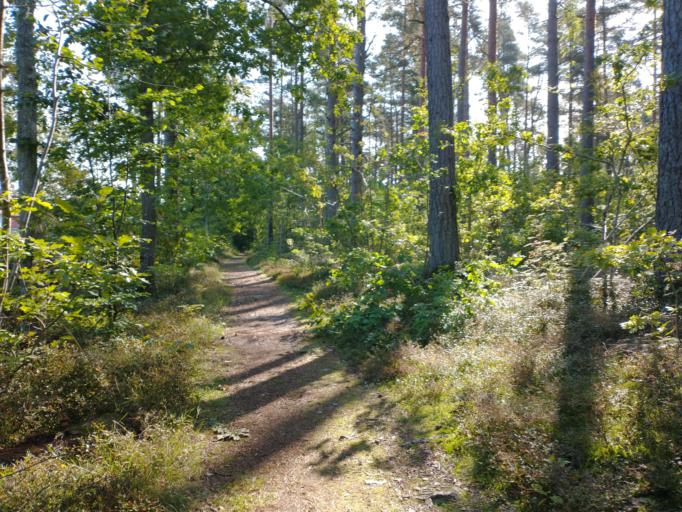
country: SE
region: Kalmar
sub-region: Kalmar Kommun
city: Lindsdal
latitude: 56.7839
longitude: 16.2869
